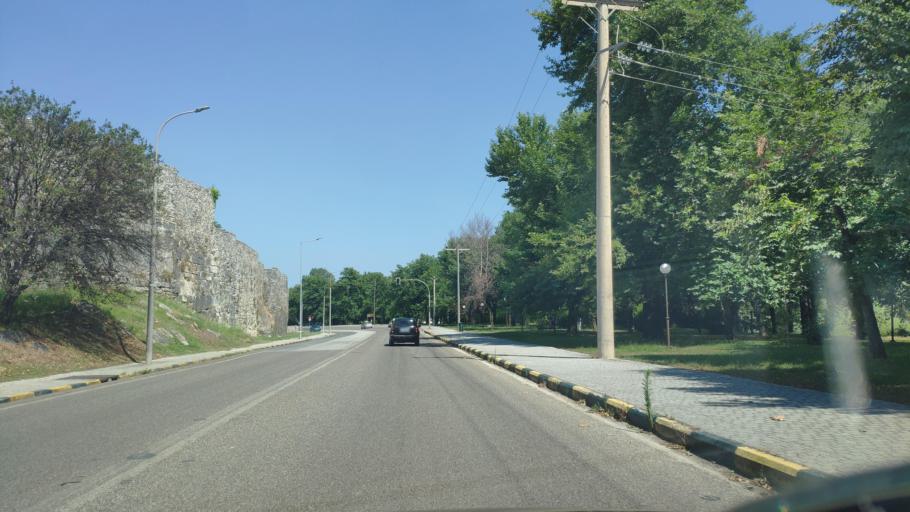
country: GR
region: Epirus
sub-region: Nomos Artas
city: Arta
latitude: 39.1657
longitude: 20.9895
